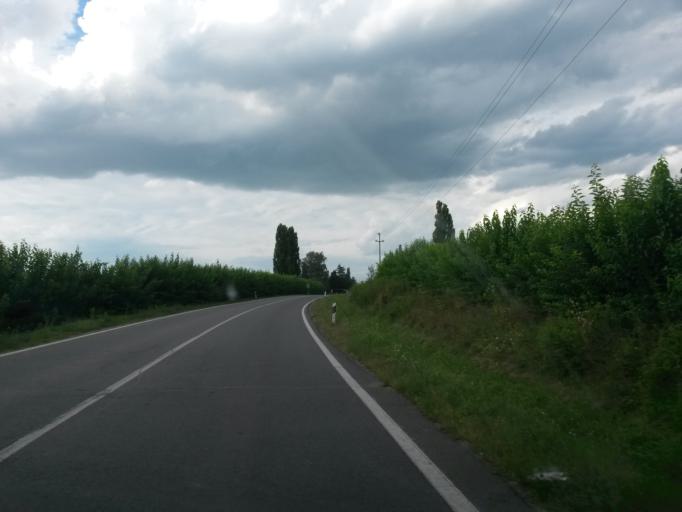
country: HR
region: Vukovarsko-Srijemska
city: Jarmina
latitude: 45.3046
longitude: 18.7351
